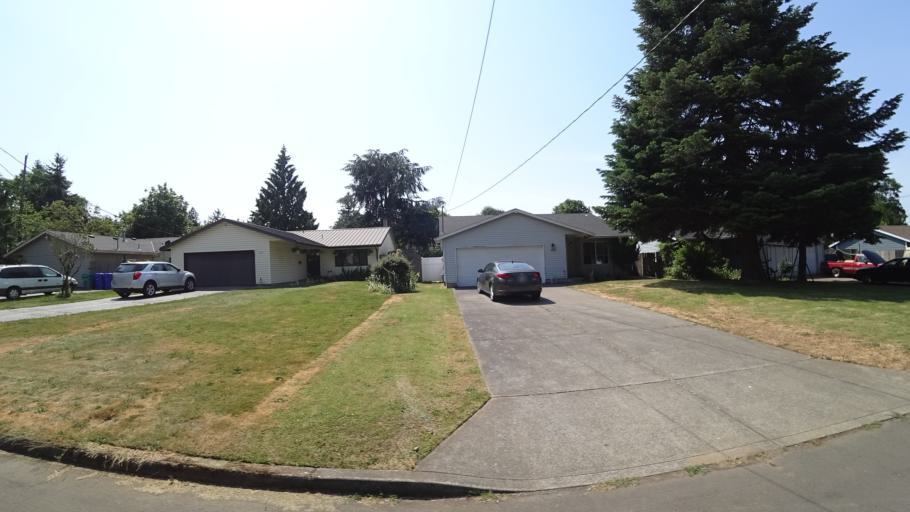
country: US
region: Oregon
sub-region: Multnomah County
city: Portland
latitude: 45.5828
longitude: -122.7066
